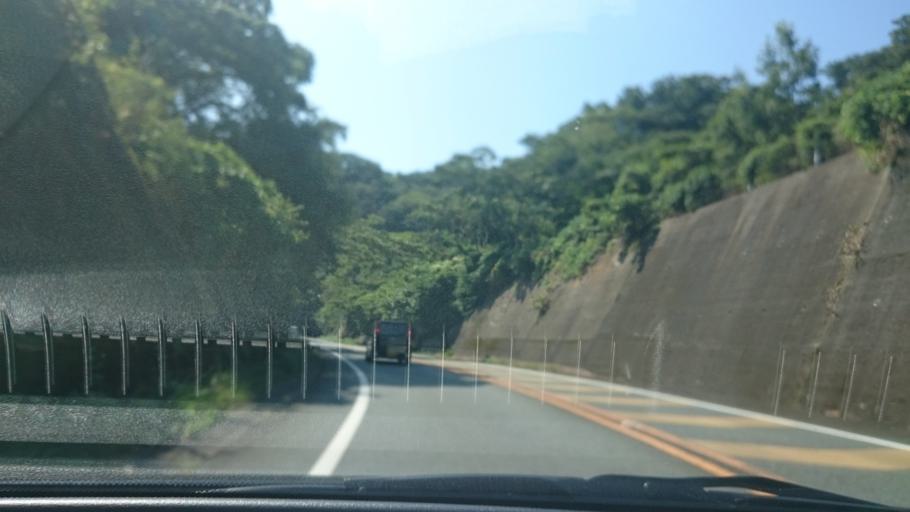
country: JP
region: Shizuoka
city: Heda
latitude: 34.8577
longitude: 138.7781
